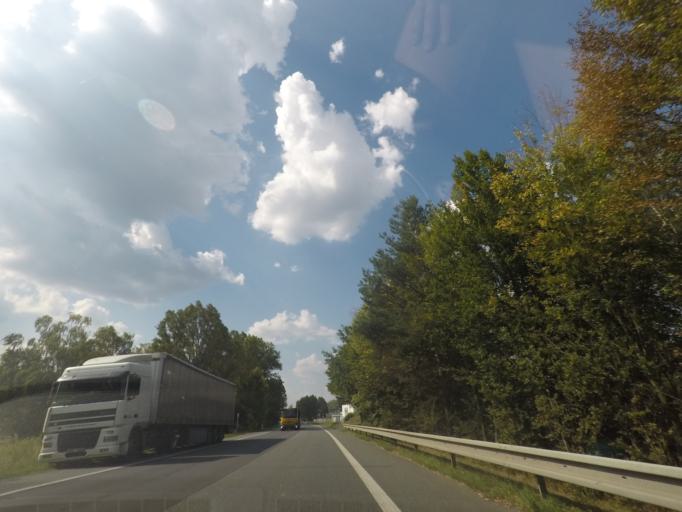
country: CZ
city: Tyniste nad Orlici
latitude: 50.1547
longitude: 16.0669
